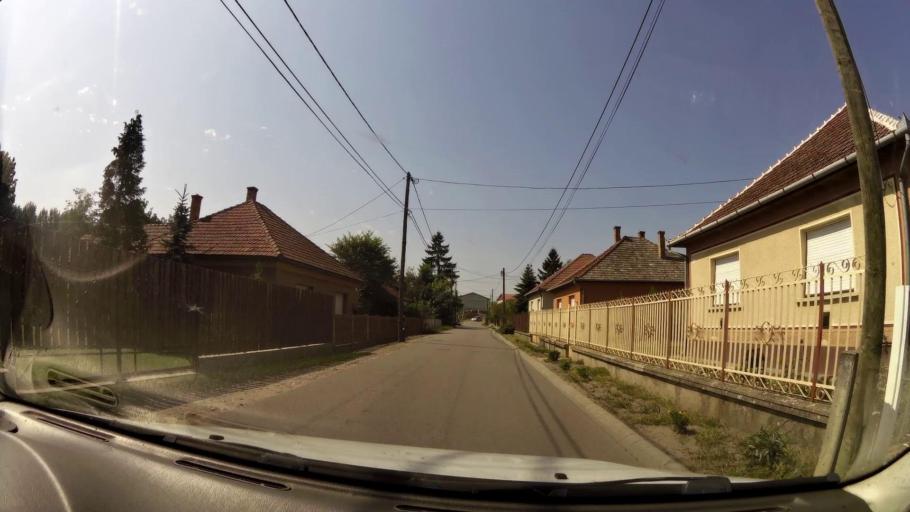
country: HU
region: Pest
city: Ujszilvas
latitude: 47.2700
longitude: 19.9183
